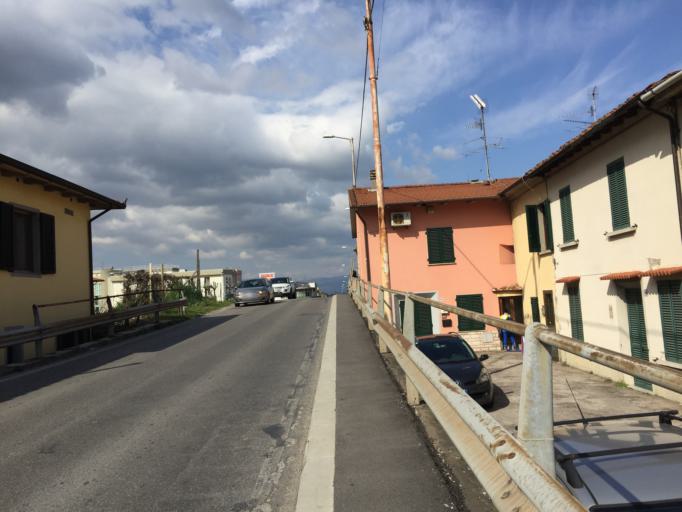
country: IT
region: Tuscany
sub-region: Provincia di Prato
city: Fornacelle
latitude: 43.8963
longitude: 11.0618
